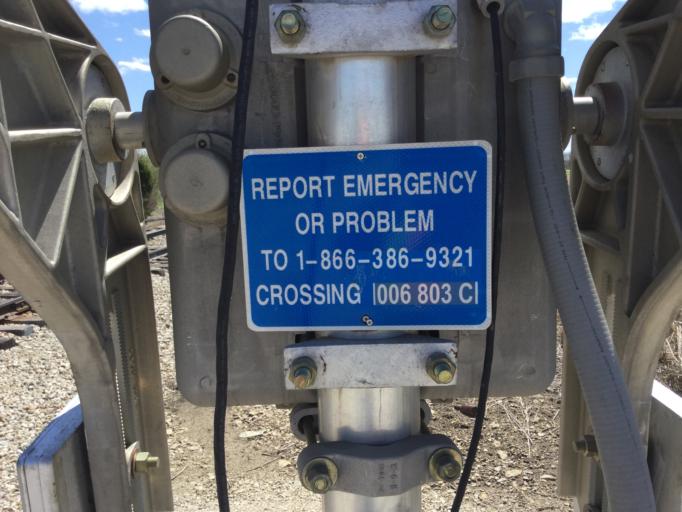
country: US
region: Kansas
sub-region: Neosho County
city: Chanute
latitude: 37.4712
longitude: -95.4747
